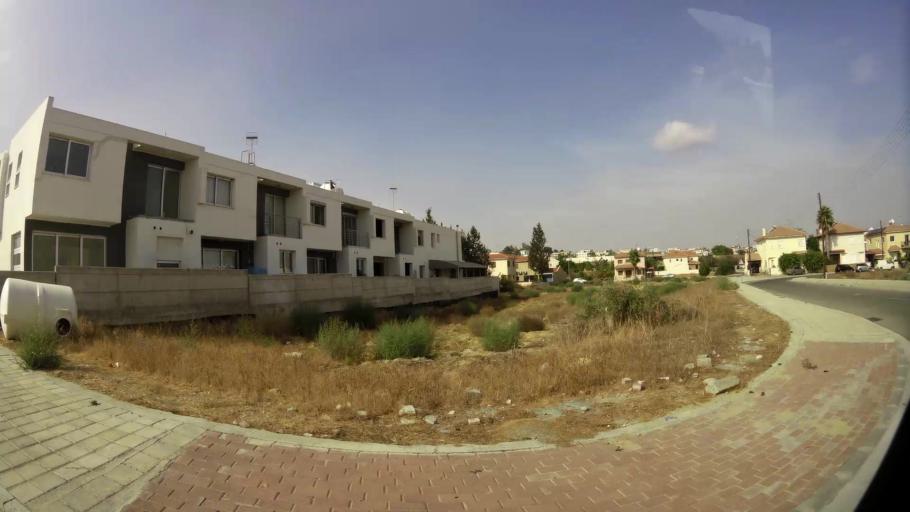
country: CY
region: Lefkosia
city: Geri
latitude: 35.0648
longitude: 33.3980
